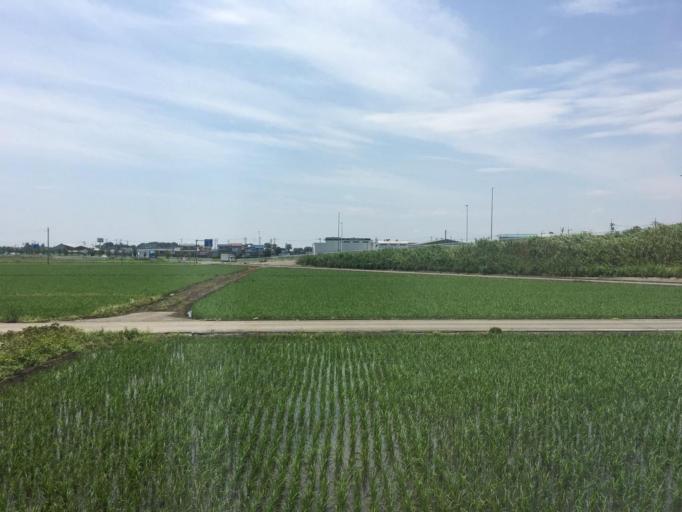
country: JP
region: Saitama
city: Menuma
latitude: 36.2578
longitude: 139.4366
